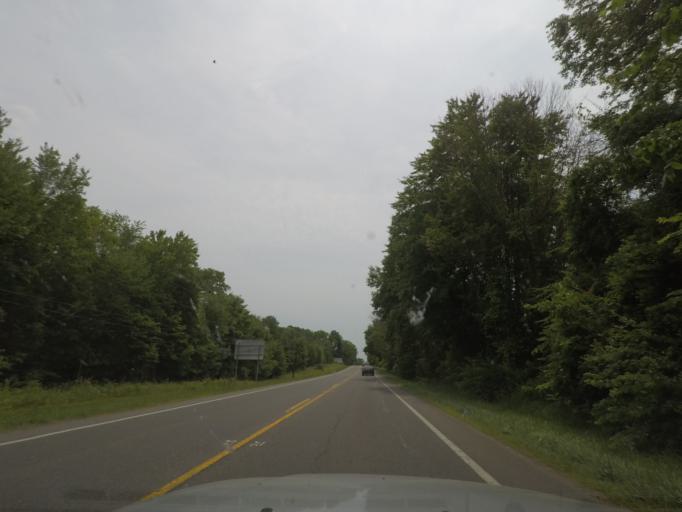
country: US
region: Virginia
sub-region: Prince William County
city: Bull Run Mountain Estates
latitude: 38.9585
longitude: -77.6224
